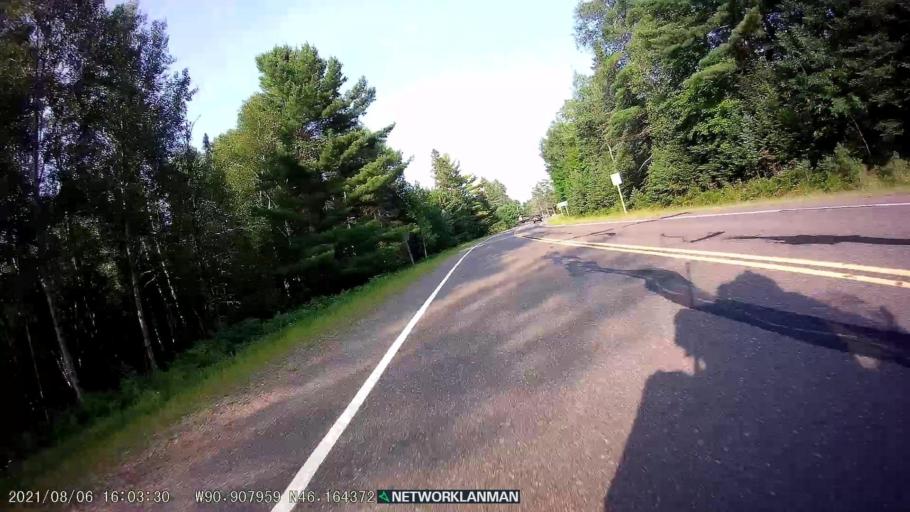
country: US
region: Wisconsin
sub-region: Ashland County
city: Ashland
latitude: 46.1643
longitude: -90.9084
